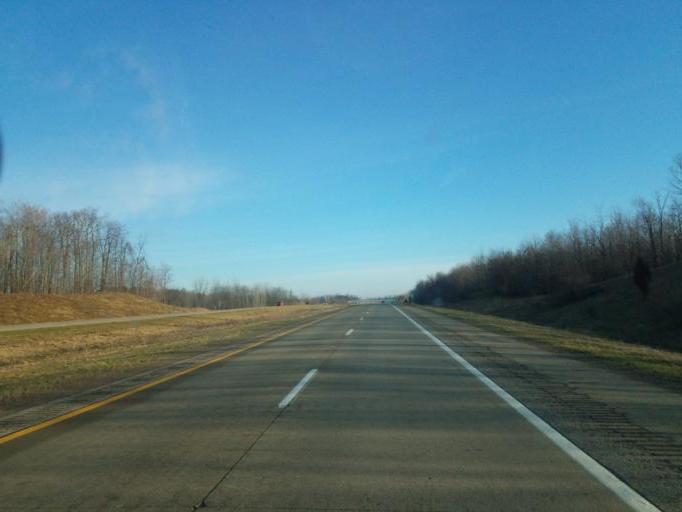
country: US
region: Michigan
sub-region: Clinton County
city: DeWitt
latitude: 42.8984
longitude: -84.5174
